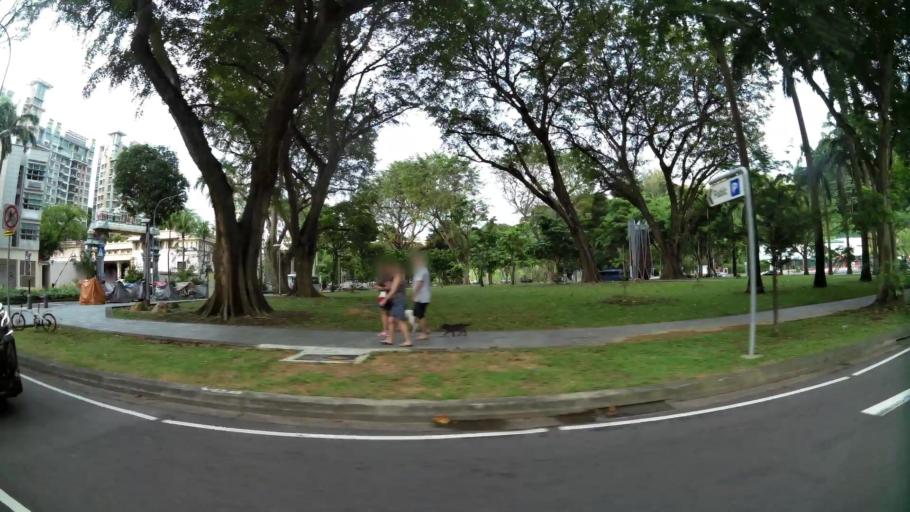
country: SG
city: Singapore
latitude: 1.2935
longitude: 103.8433
